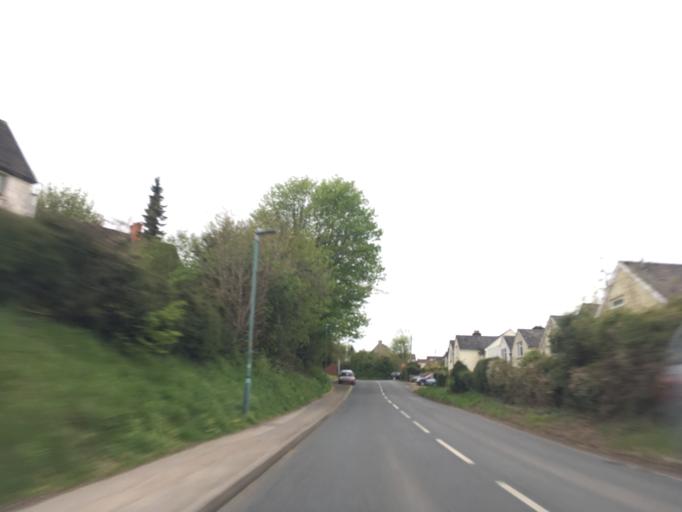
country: GB
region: England
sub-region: Gloucestershire
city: Nailsworth
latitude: 51.6976
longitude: -2.2257
